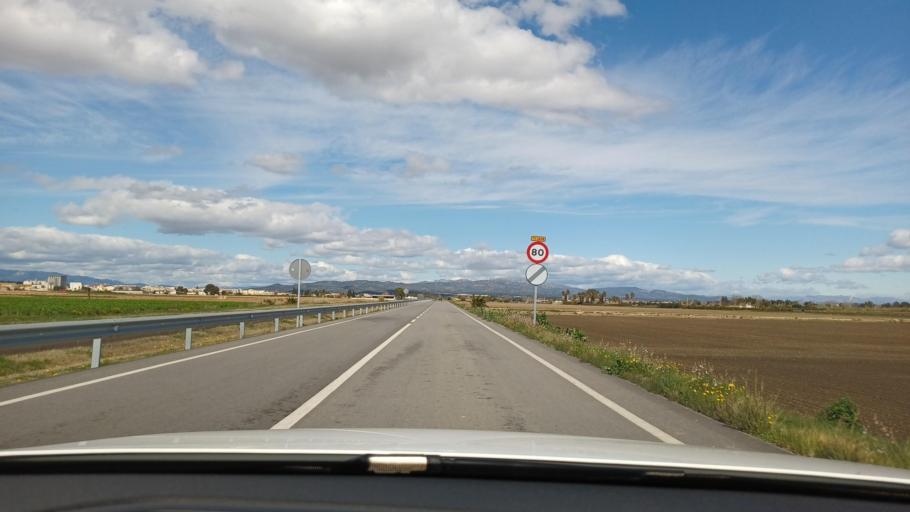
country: ES
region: Catalonia
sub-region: Provincia de Tarragona
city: Amposta
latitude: 40.6843
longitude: 0.5905
